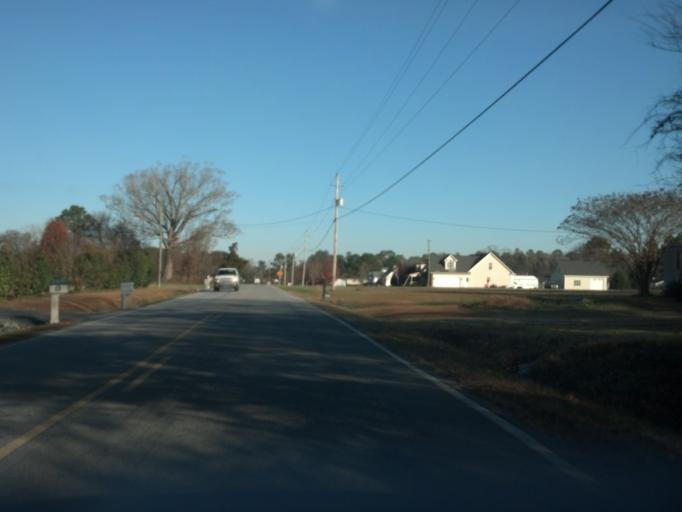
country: US
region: North Carolina
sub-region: Pitt County
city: Winterville
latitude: 35.5252
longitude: -77.4421
